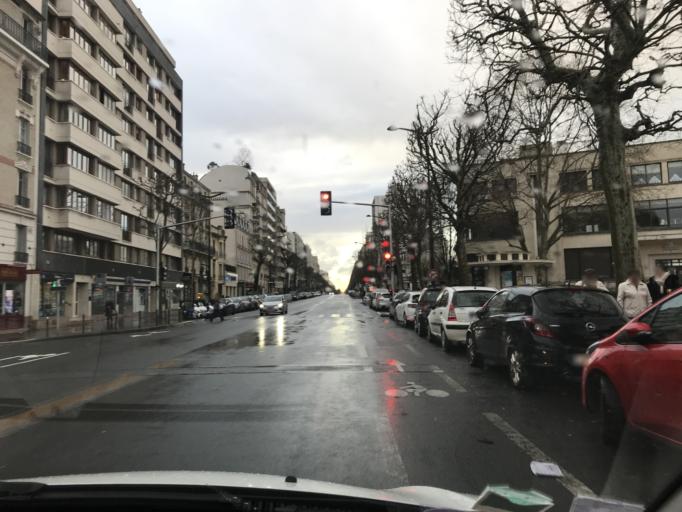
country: FR
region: Ile-de-France
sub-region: Departement du Val-de-Marne
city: Charenton-le-Pont
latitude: 48.8216
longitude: 2.4136
